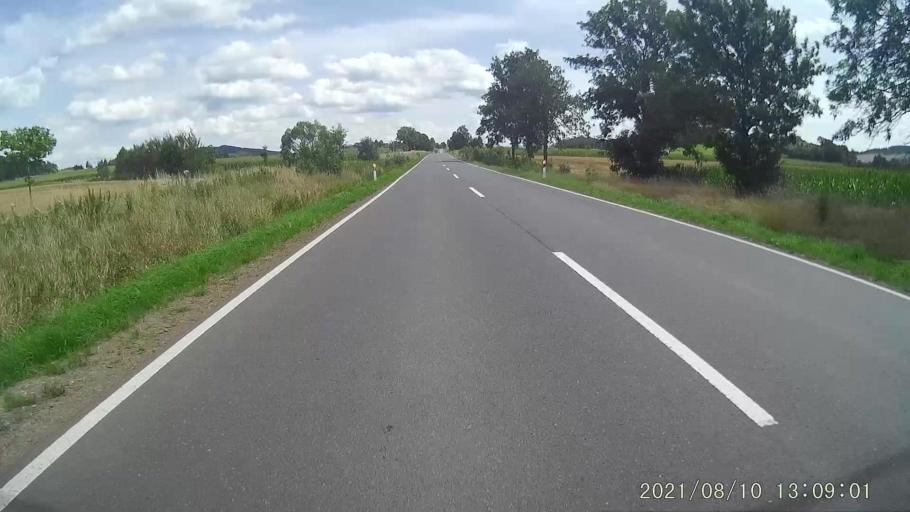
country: PL
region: Lower Silesian Voivodeship
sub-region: Powiat klodzki
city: Bozkow
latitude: 50.4962
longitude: 16.5462
